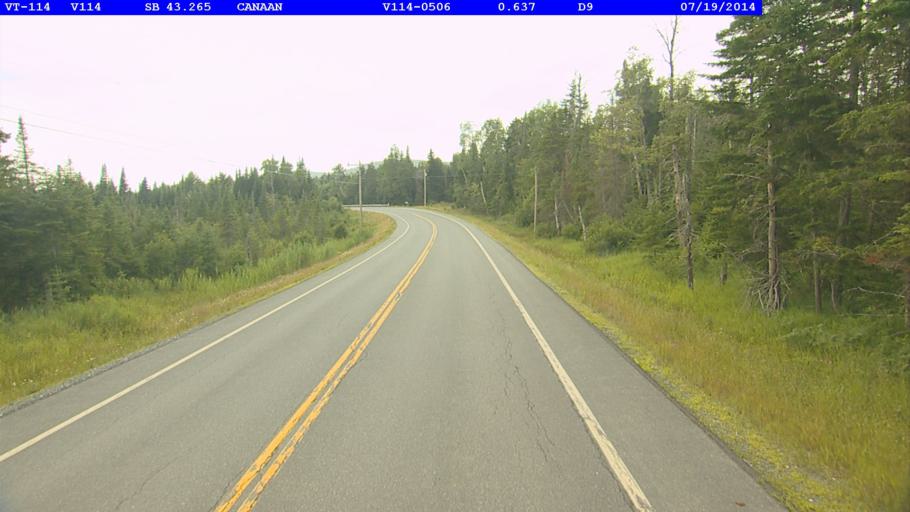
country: CA
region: Quebec
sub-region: Estrie
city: Coaticook
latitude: 45.0063
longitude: -71.6808
